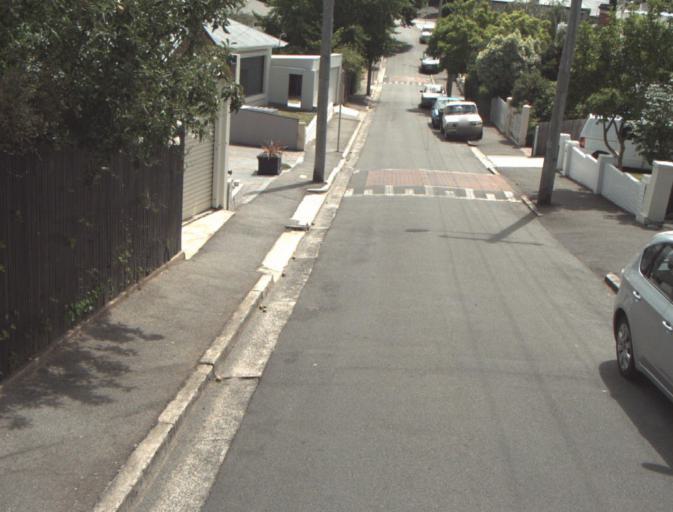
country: AU
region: Tasmania
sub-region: Launceston
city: East Launceston
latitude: -41.4368
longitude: 147.1522
